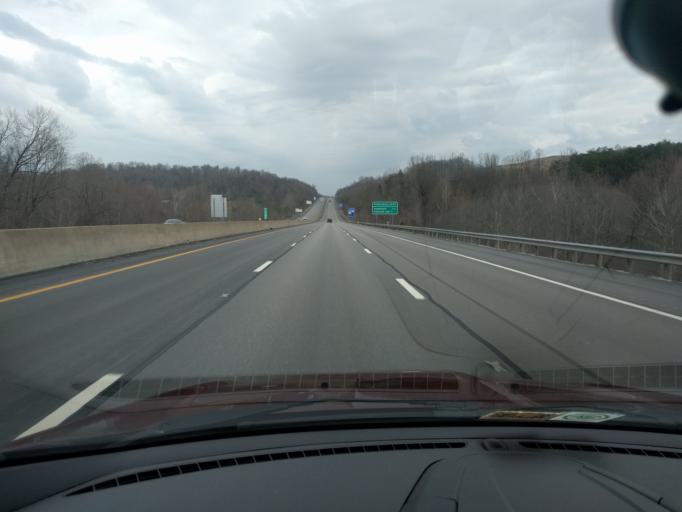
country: US
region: West Virginia
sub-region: Wood County
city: Mineral Wells
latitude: 39.2434
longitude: -81.5001
